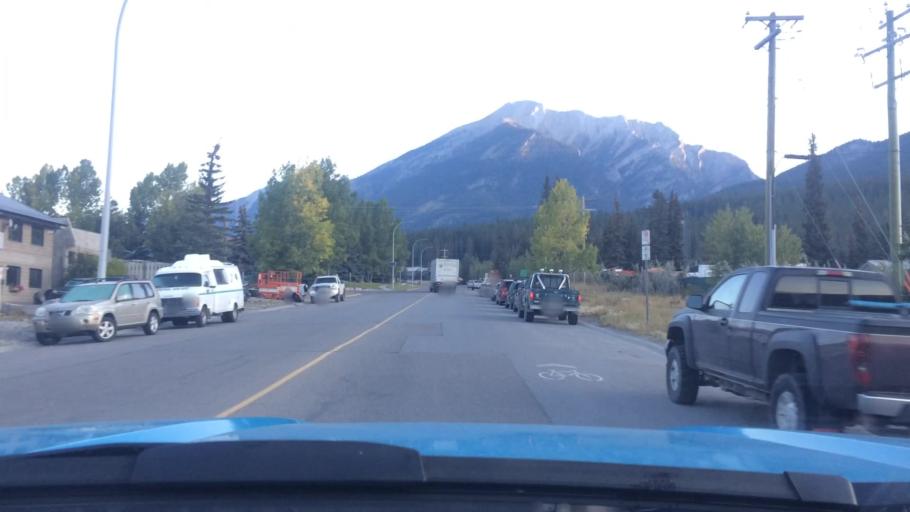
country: CA
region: Alberta
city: Canmore
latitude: 51.0777
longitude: -115.3212
